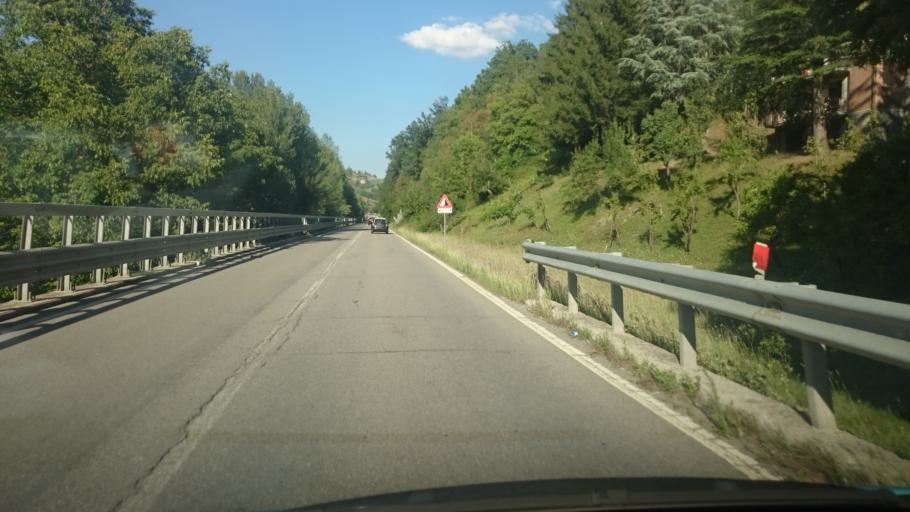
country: IT
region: Emilia-Romagna
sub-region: Provincia di Reggio Emilia
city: Villa Minozzo
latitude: 44.4023
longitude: 10.4940
